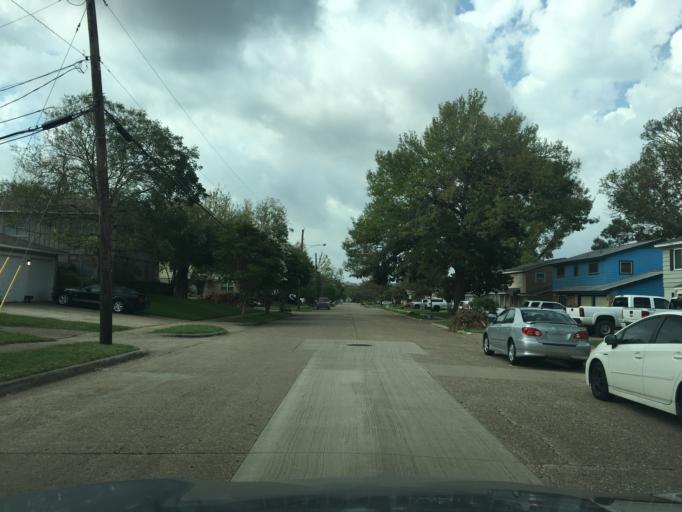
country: US
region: Texas
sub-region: Dallas County
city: Richardson
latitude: 32.9026
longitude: -96.7604
